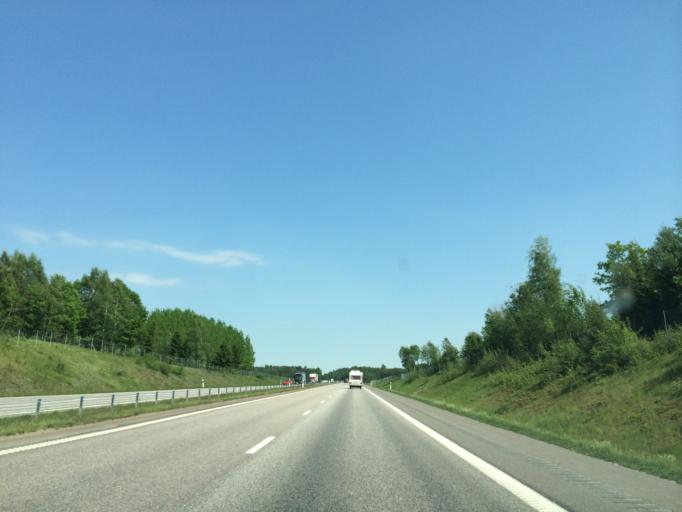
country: SE
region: OEstergoetland
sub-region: Linkopings Kommun
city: Linghem
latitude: 58.4497
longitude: 15.7455
